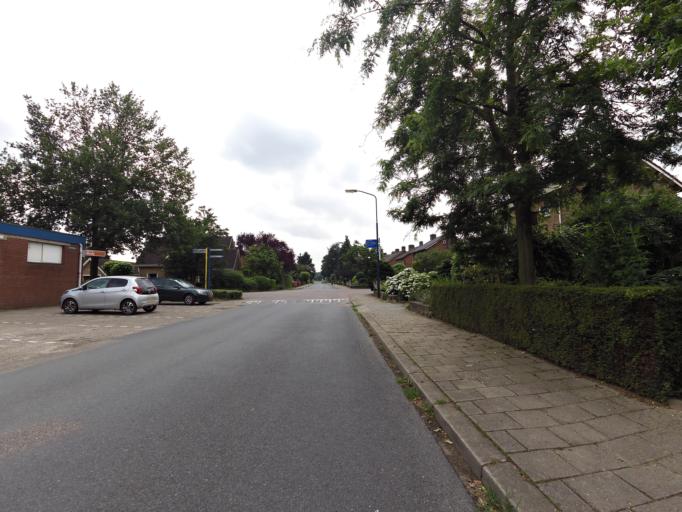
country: NL
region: Gelderland
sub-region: Gemeente Doetinchem
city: Doetinchem
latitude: 51.9570
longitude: 6.2085
